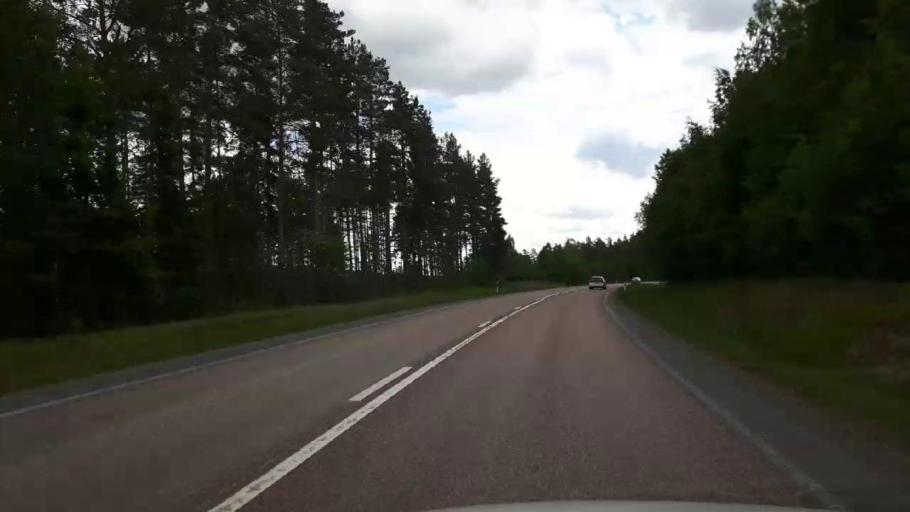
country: SE
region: Dalarna
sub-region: Saters Kommun
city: Saeter
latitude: 60.4697
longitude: 15.7968
